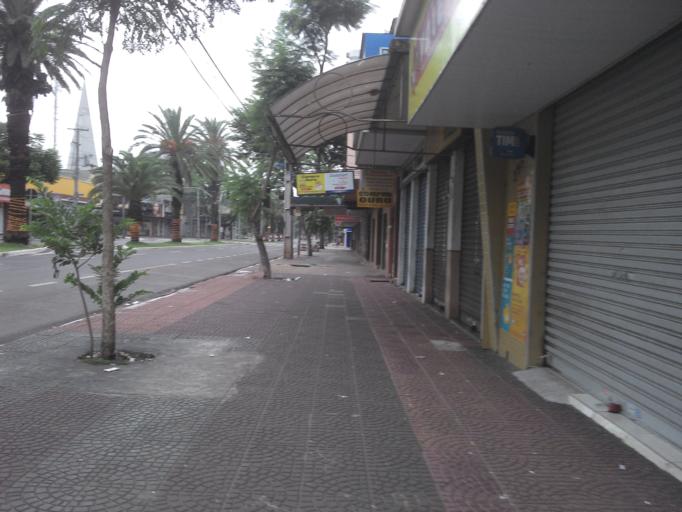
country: BR
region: Parana
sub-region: Maringa
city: Maringa
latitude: -23.4219
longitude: -51.9401
